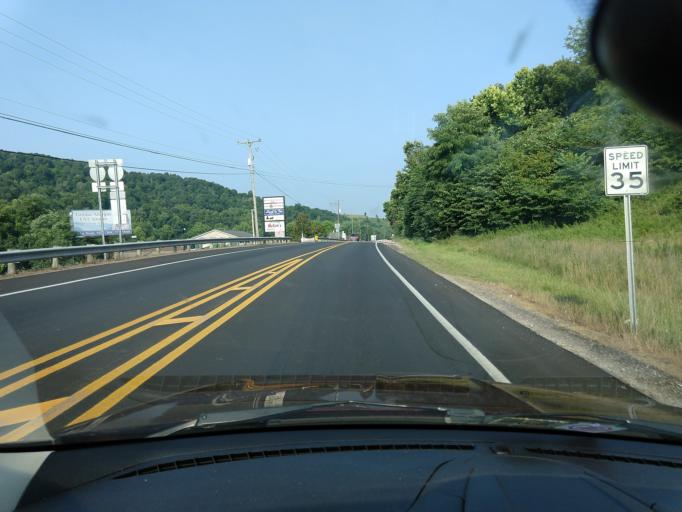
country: US
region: West Virginia
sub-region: Jackson County
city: Ripley
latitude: 38.8194
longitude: -81.7302
